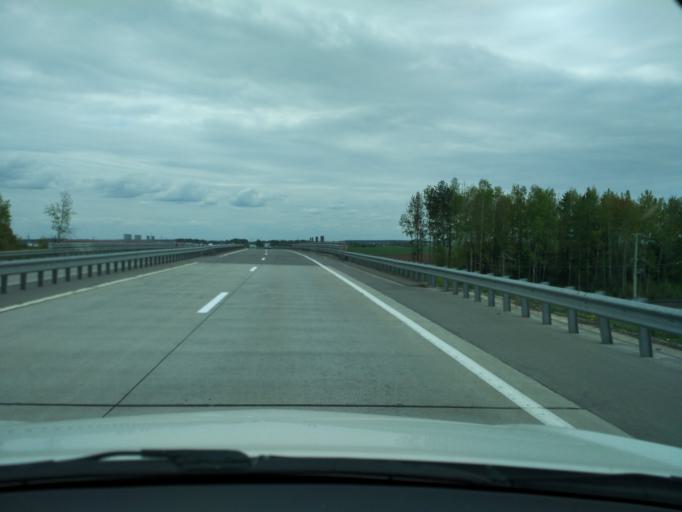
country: BY
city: Fanipol
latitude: 53.7669
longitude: 27.3686
